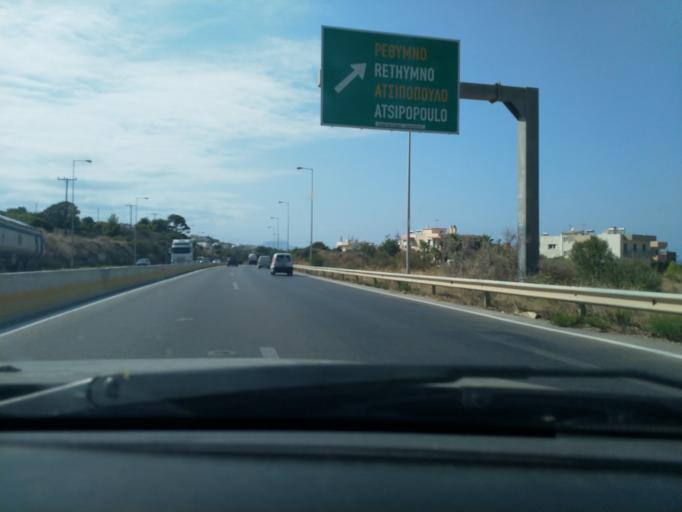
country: GR
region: Crete
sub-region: Nomos Rethymnis
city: Atsipopoulon
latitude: 35.3599
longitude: 24.4499
